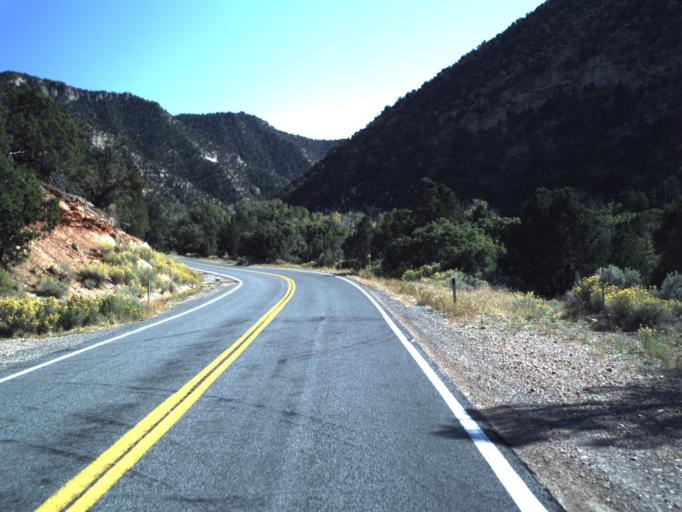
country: US
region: Utah
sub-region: Iron County
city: Parowan
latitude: 37.8235
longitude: -112.8114
